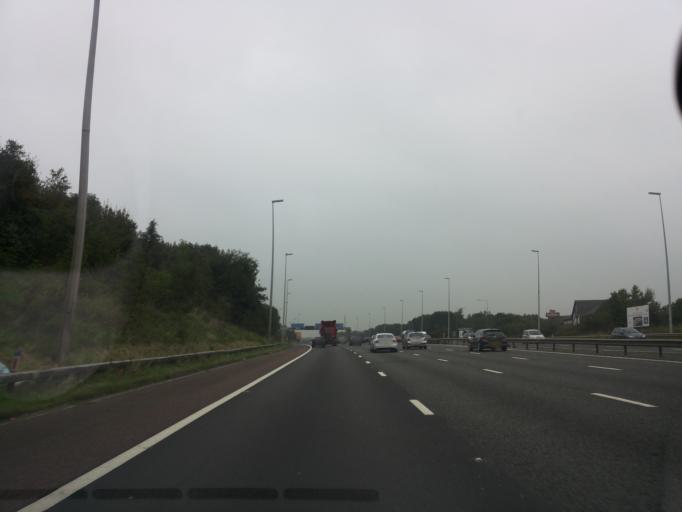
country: GB
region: England
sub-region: Lancashire
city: Goosnargh
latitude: 53.7881
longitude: -2.6570
